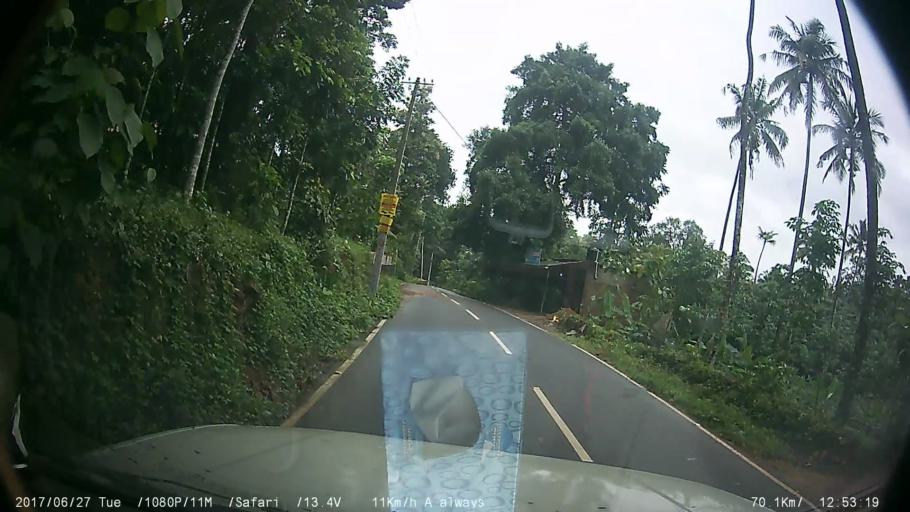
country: IN
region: Kerala
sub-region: Kottayam
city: Palackattumala
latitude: 9.7805
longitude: 76.5433
